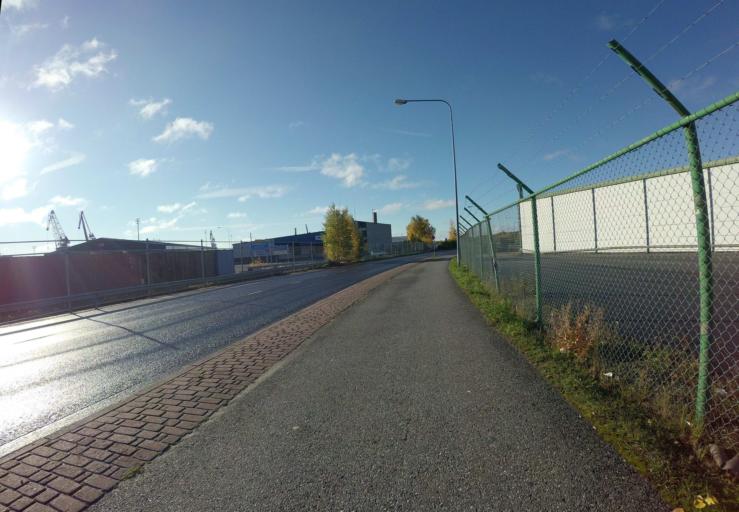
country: FI
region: Varsinais-Suomi
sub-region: Turku
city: Turku
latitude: 60.4448
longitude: 22.2149
